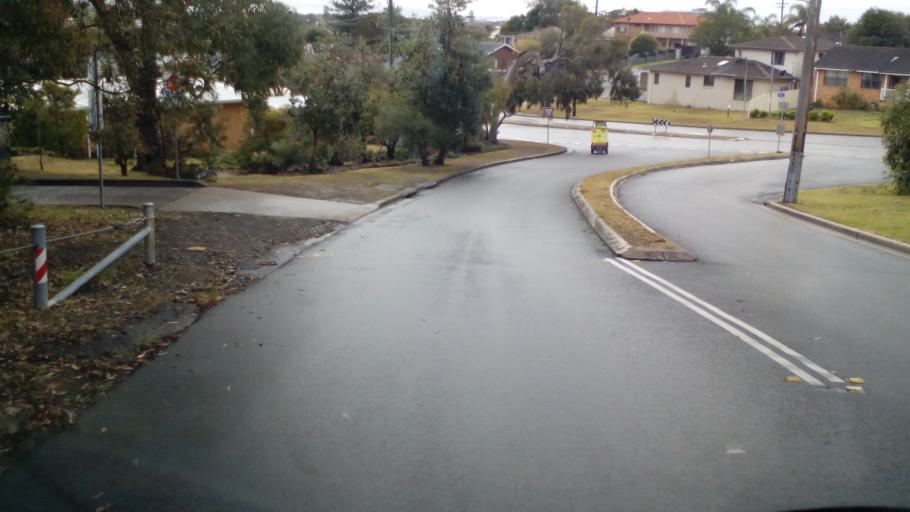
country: AU
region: New South Wales
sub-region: Lake Macquarie Shire
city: Belmont South
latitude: -33.1079
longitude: 151.6403
